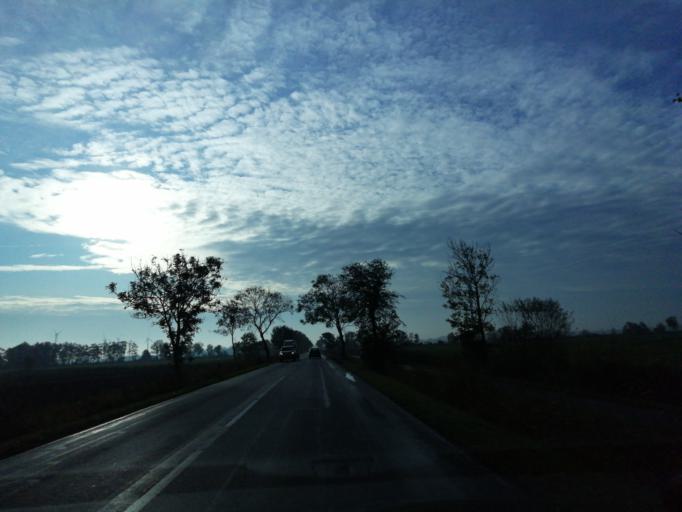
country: DE
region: Lower Saxony
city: Fedderwarden
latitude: 53.6138
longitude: 8.0399
